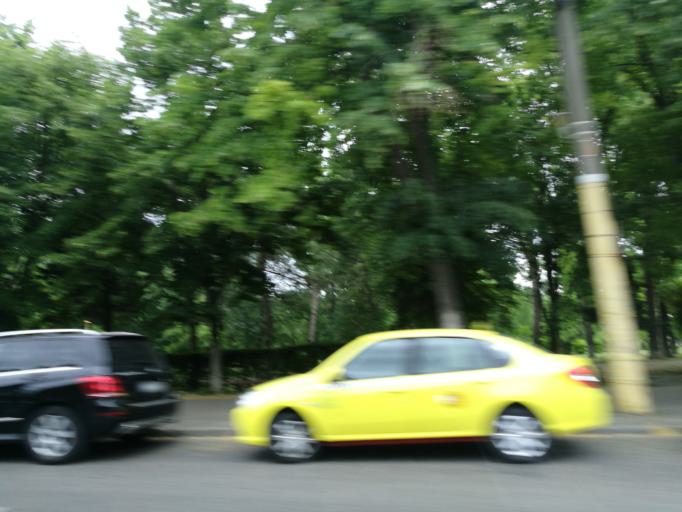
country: RO
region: Constanta
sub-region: Municipiul Constanta
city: Constanta
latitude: 44.2085
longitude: 28.6290
